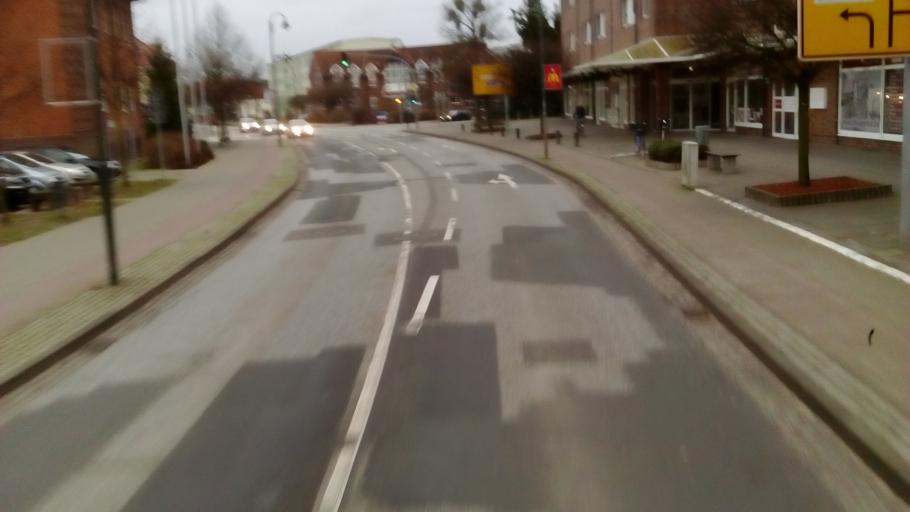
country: DE
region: Brandenburg
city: Brussow
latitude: 53.4532
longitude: 14.2135
